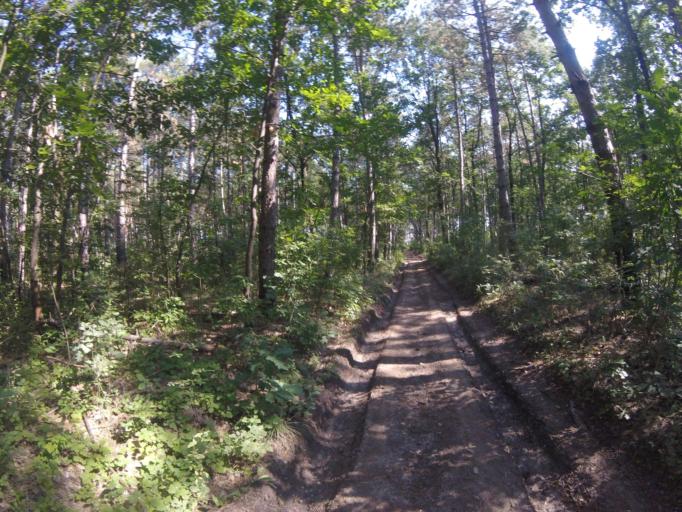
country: HU
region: Nograd
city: Bujak
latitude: 47.8907
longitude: 19.5424
